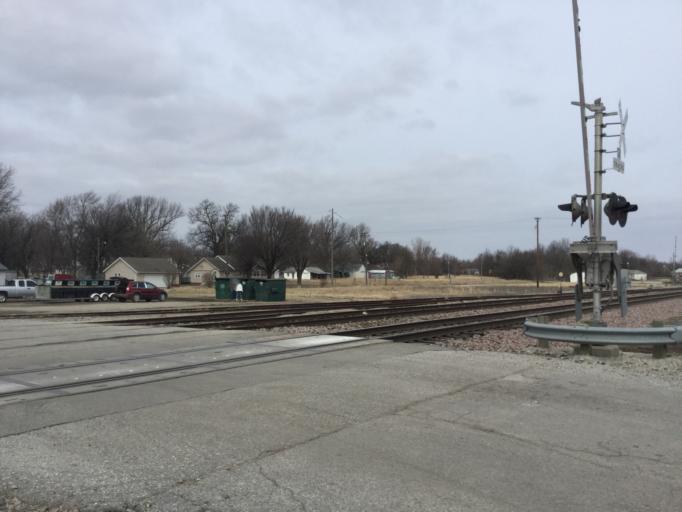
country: US
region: Kansas
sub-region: Cherokee County
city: Columbus
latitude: 37.1718
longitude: -94.8380
